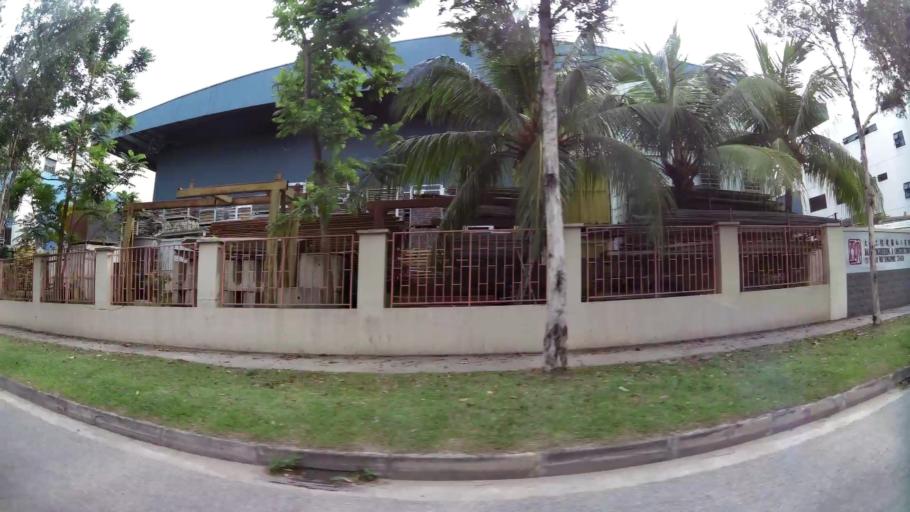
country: MY
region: Johor
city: Johor Bahru
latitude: 1.4364
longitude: 103.7469
